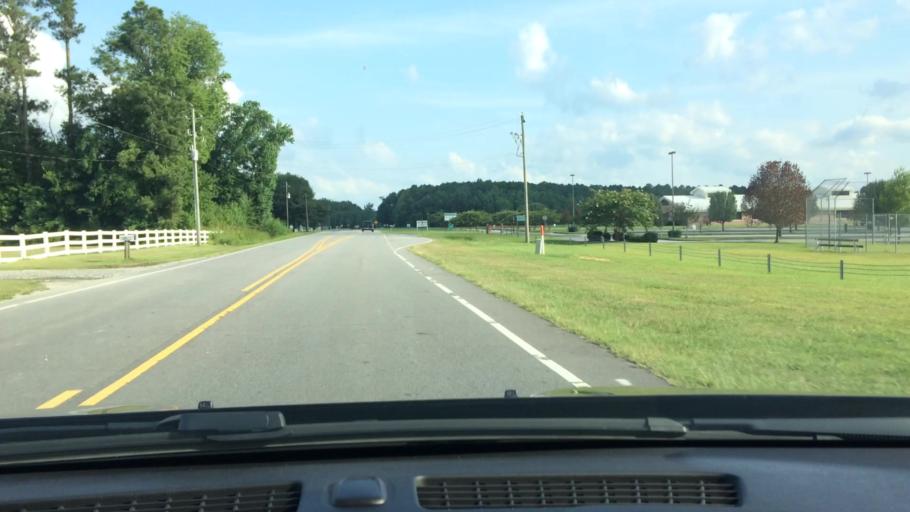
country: US
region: North Carolina
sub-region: Beaufort County
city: River Road
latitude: 35.4479
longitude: -77.0554
